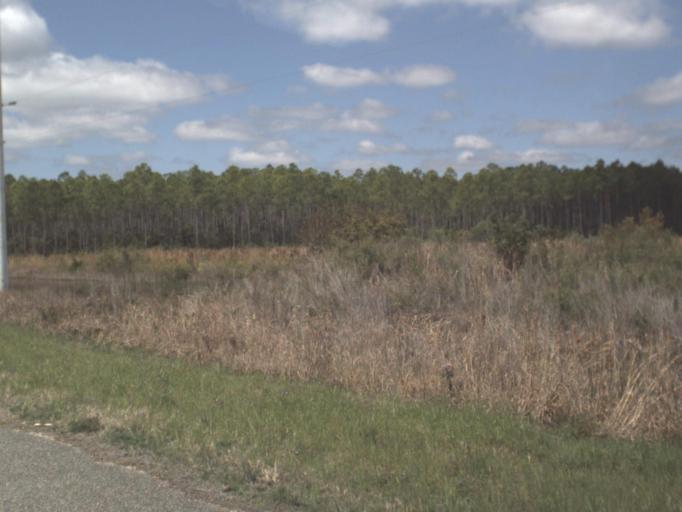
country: US
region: Florida
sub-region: Franklin County
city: Apalachicola
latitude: 29.7233
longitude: -85.0965
